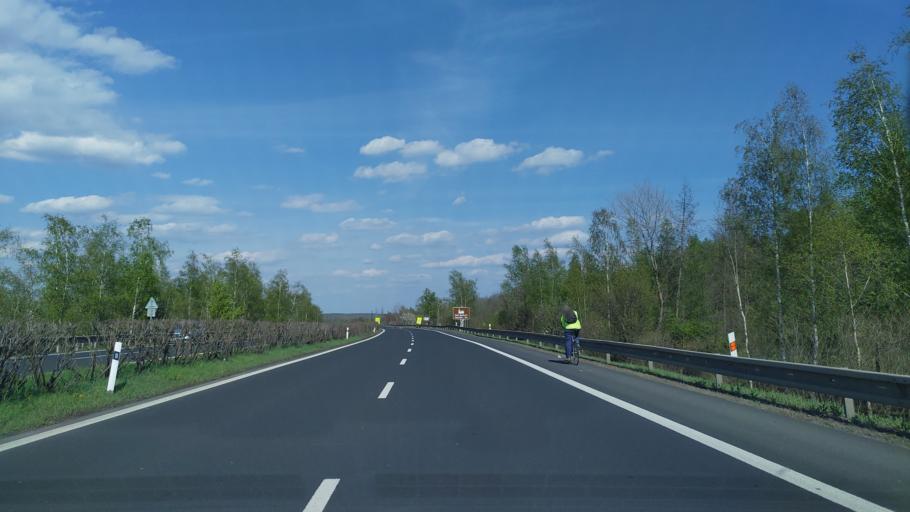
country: CZ
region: Ustecky
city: Horni Jiretin
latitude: 50.5204
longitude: 13.5373
